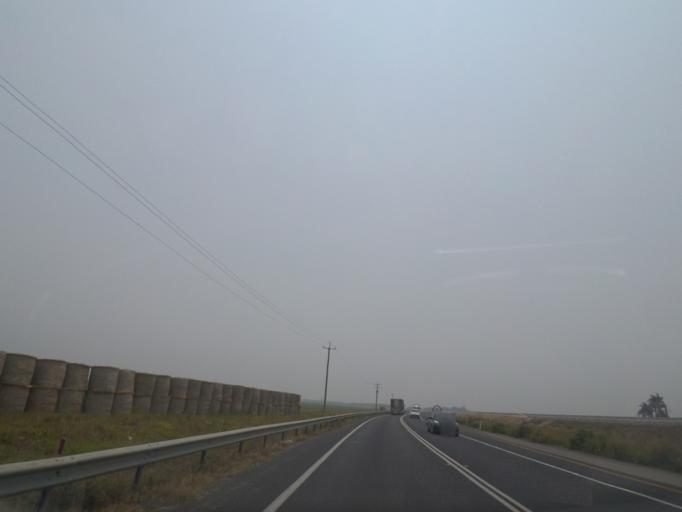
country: AU
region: New South Wales
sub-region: Clarence Valley
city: Maclean
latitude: -29.4148
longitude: 153.2411
